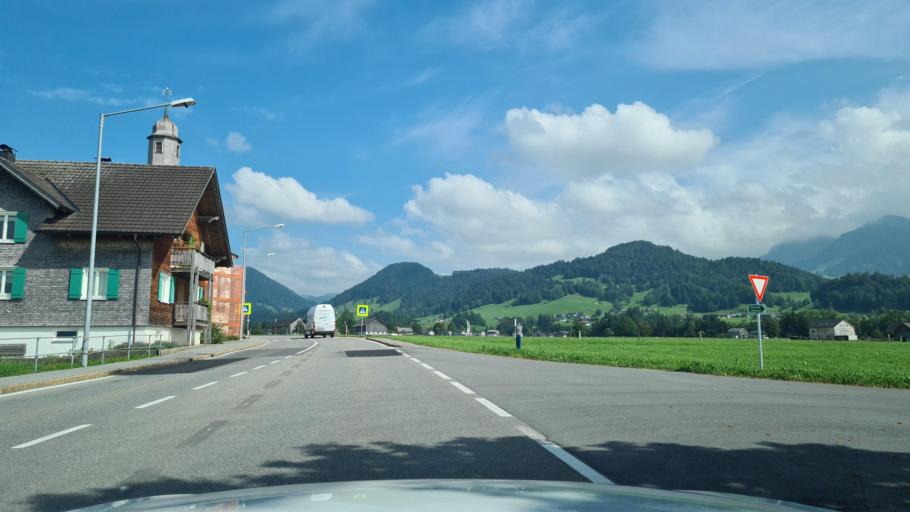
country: AT
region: Vorarlberg
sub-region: Politischer Bezirk Bregenz
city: Egg
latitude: 47.4478
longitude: 9.9105
